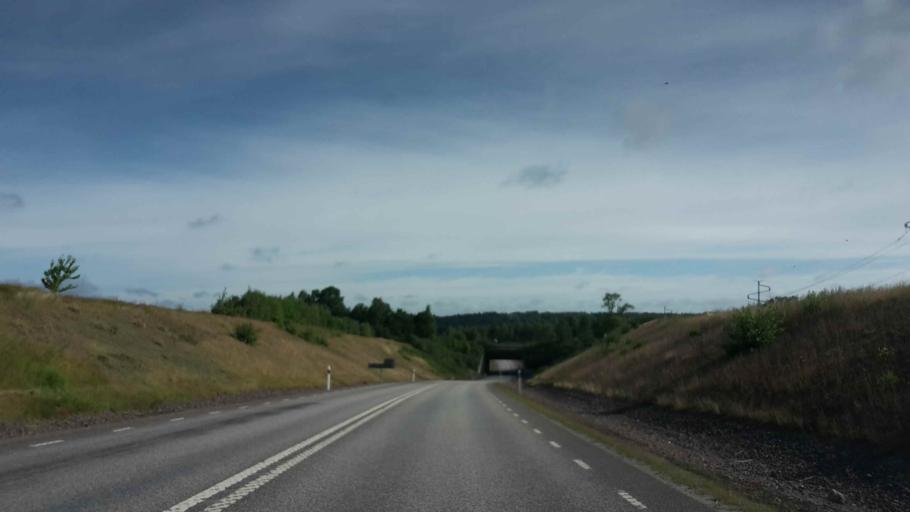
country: SE
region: OEstergoetland
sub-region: Motala Kommun
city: Borensberg
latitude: 58.5478
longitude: 15.3206
